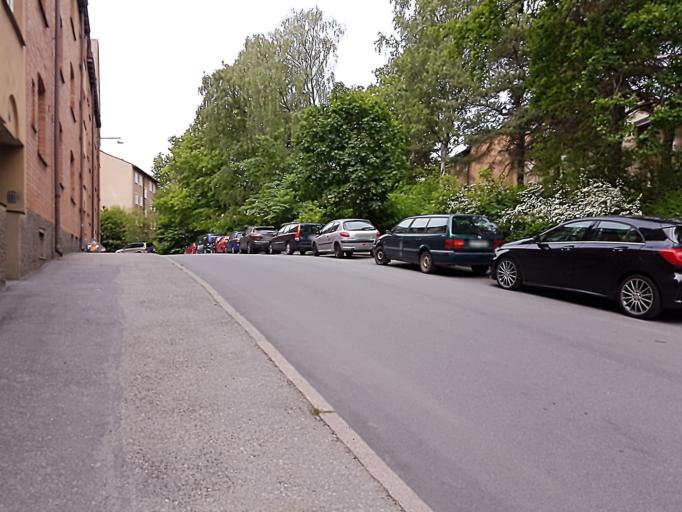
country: SE
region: Stockholm
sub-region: Solna Kommun
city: Rasunda
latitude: 59.3631
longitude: 17.9830
